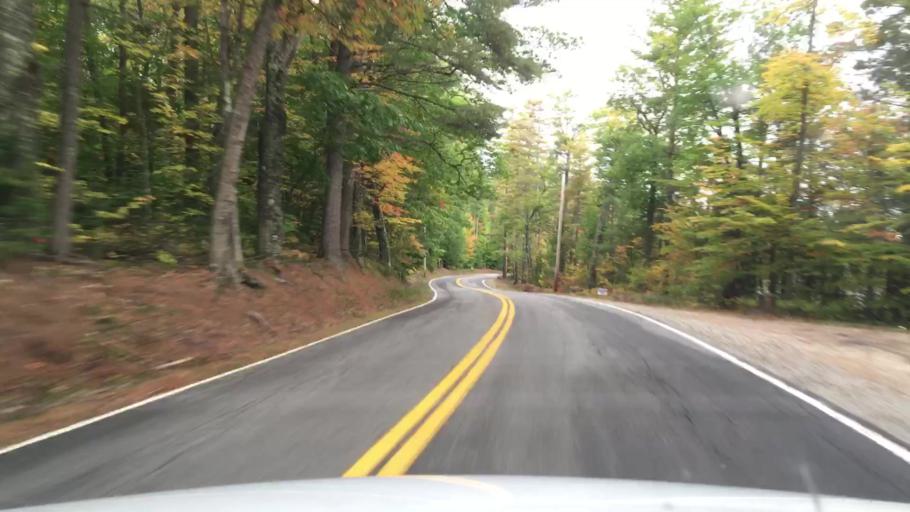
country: US
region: Maine
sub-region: Oxford County
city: Bethel
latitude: 44.3540
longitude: -70.7917
